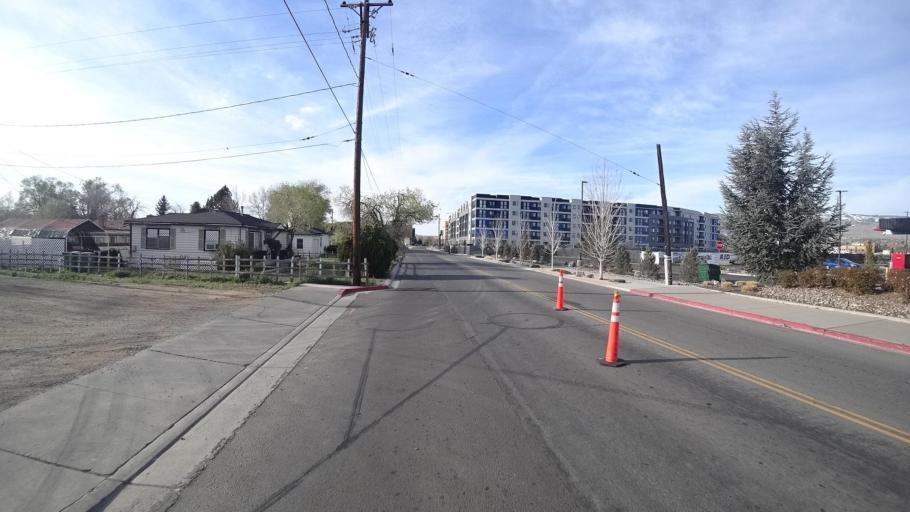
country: US
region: Nevada
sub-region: Washoe County
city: Reno
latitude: 39.5054
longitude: -119.7982
